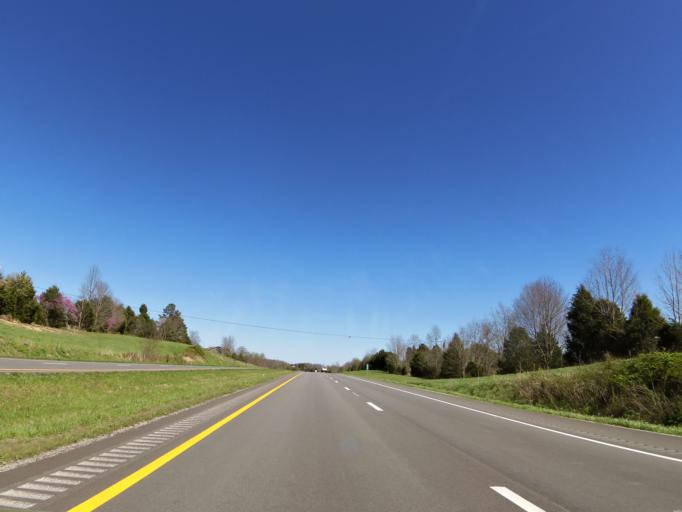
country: US
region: Kentucky
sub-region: Pulaski County
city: Somerset
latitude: 37.0974
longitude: -84.7367
